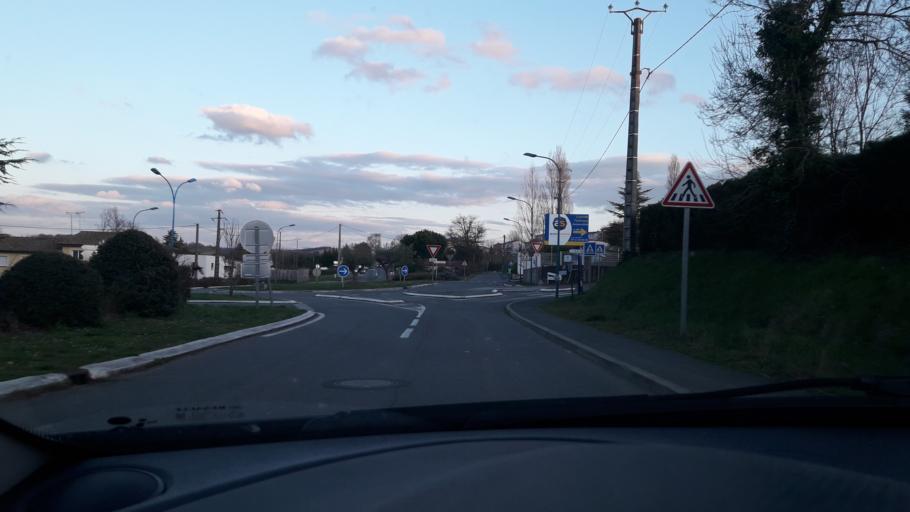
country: FR
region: Midi-Pyrenees
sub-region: Departement du Gers
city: Pujaudran
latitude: 43.6047
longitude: 1.1006
